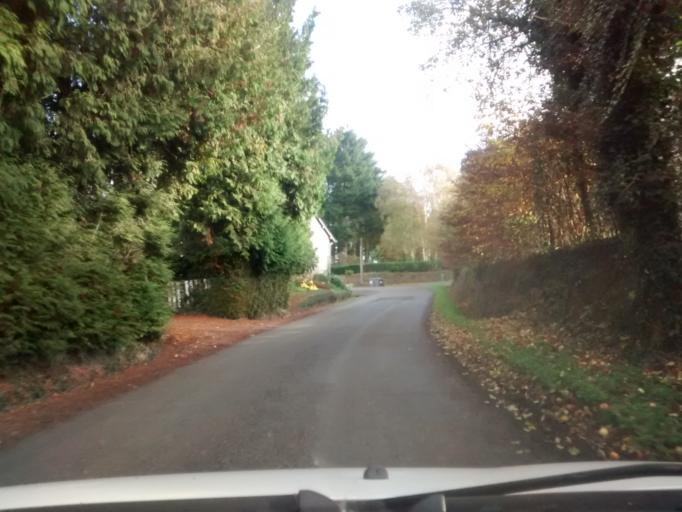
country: FR
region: Brittany
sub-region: Departement d'Ille-et-Vilaine
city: Servon-sur-Vilaine
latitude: 48.1311
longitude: -1.4755
